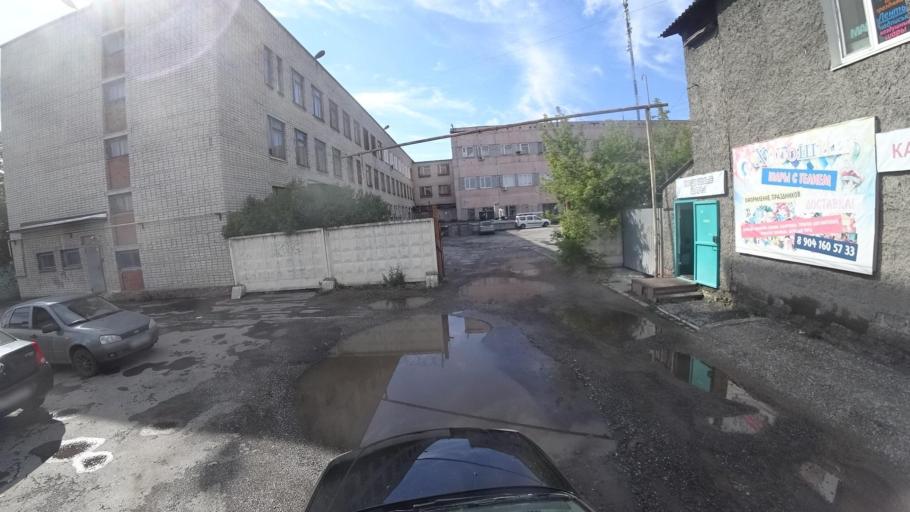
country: RU
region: Sverdlovsk
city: Kamyshlov
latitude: 56.8427
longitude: 62.7104
